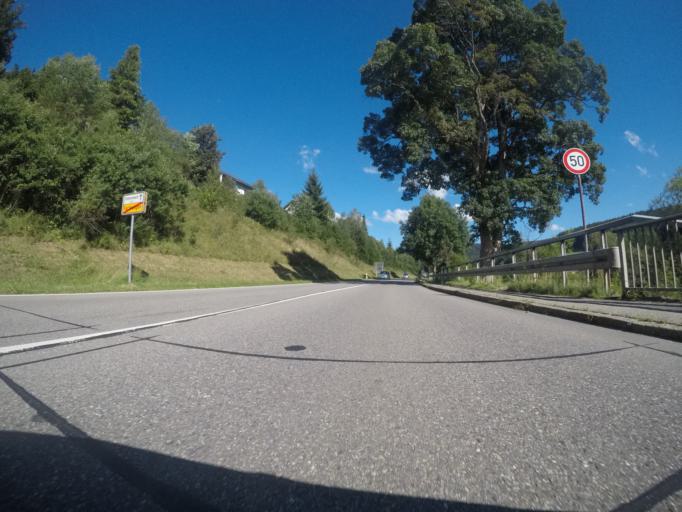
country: DE
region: Baden-Wuerttemberg
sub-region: Freiburg Region
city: Furtwangen im Schwarzwald
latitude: 48.0479
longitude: 8.2209
